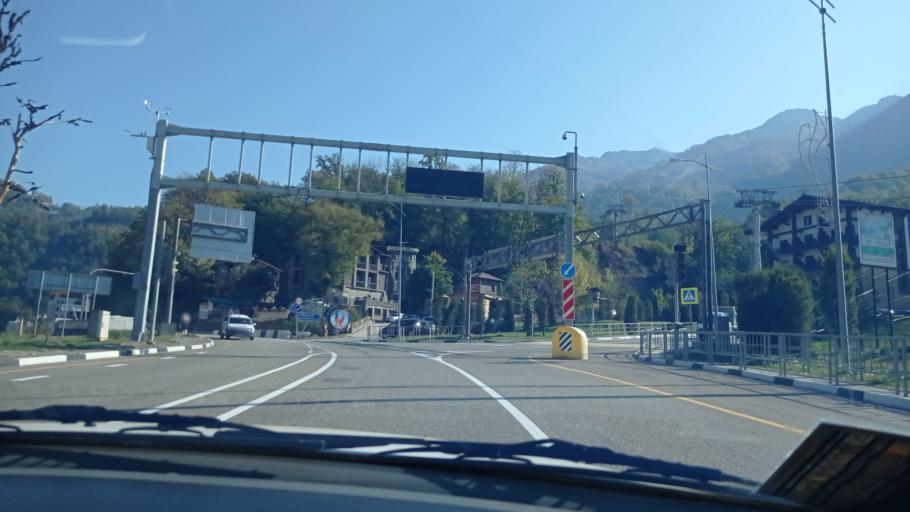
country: RU
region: Krasnodarskiy
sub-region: Sochi City
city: Krasnaya Polyana
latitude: 43.6759
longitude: 40.2848
